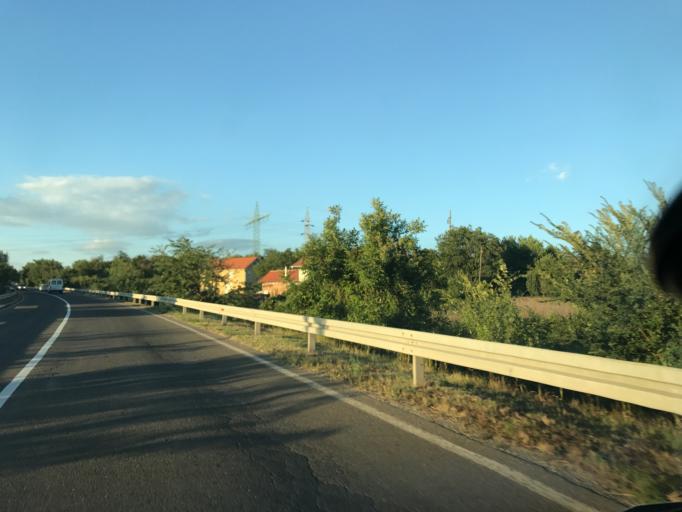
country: RS
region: Central Serbia
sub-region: Branicevski Okrug
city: Pozarevac
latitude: 44.6509
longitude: 21.1915
